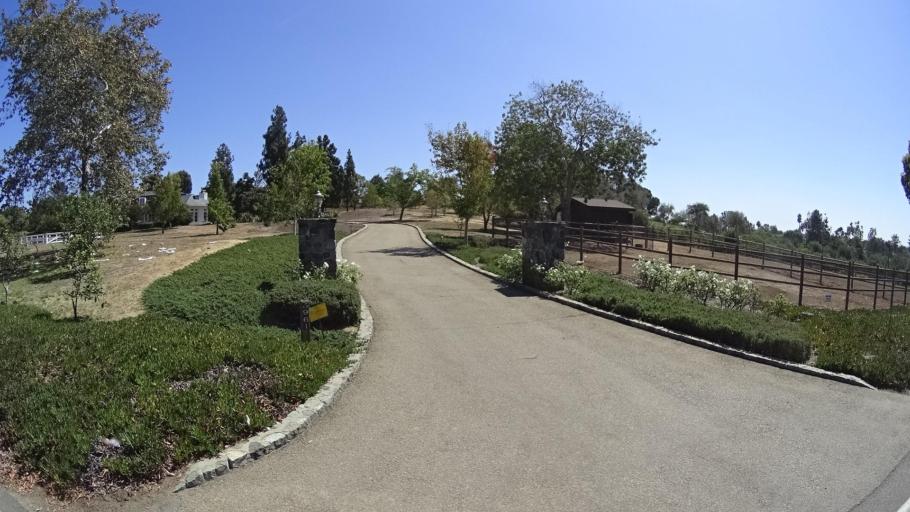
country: US
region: California
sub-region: San Diego County
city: Rancho Santa Fe
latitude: 33.0328
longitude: -117.2054
